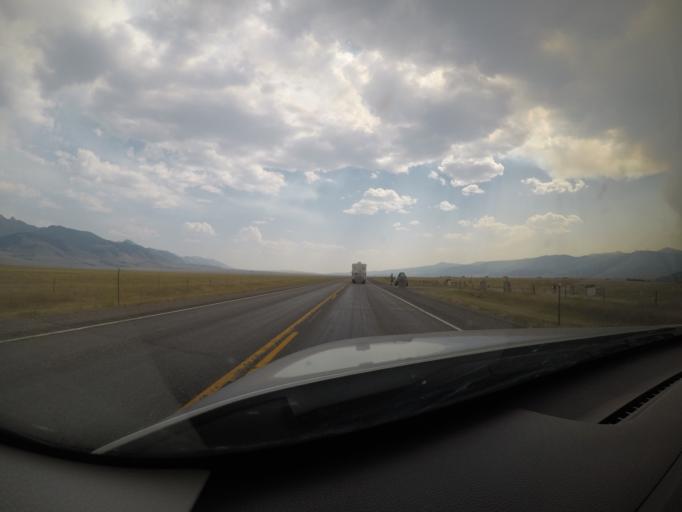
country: US
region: Montana
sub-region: Gallatin County
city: Big Sky
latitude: 45.0724
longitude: -111.6460
